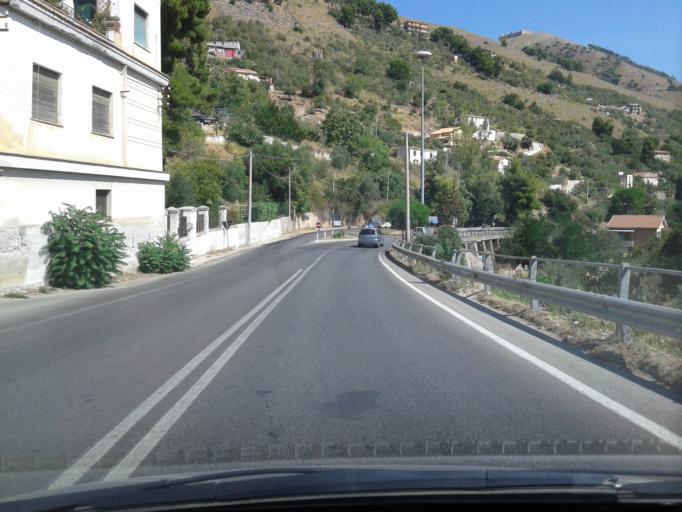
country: IT
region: Sicily
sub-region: Palermo
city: Cannizzaro-Favara
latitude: 38.0693
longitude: 13.2691
